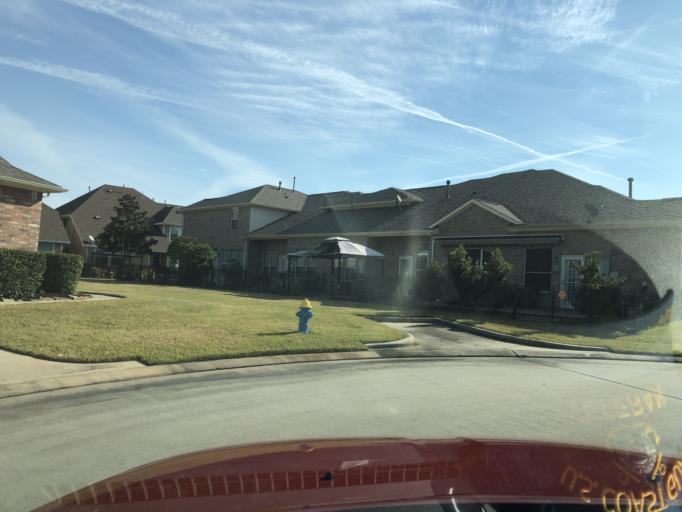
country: US
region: Texas
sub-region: Harris County
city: Tomball
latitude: 30.0366
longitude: -95.5549
